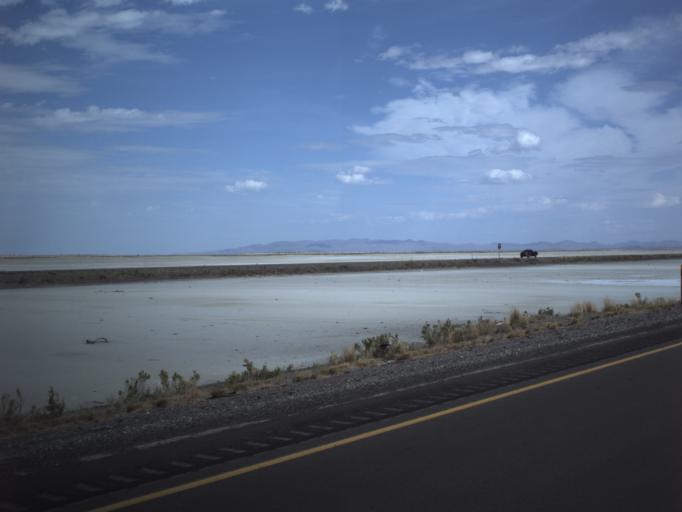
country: US
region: Utah
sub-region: Tooele County
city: Wendover
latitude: 40.7301
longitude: -113.4657
